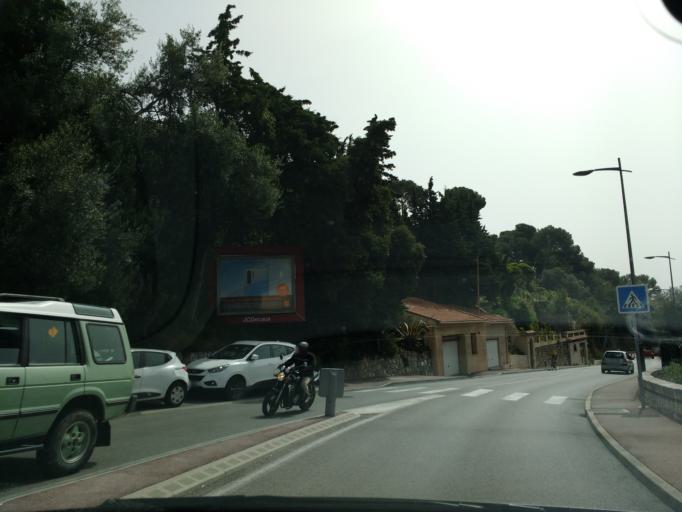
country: FR
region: Provence-Alpes-Cote d'Azur
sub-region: Departement des Alpes-Maritimes
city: Roquebrune-Cap-Martin
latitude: 43.7614
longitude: 7.4742
